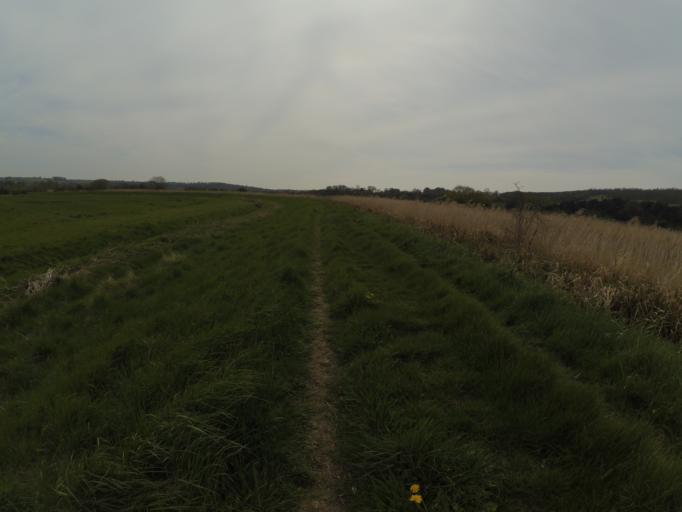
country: GB
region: England
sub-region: West Sussex
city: Arundel
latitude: 50.8752
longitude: -0.5407
